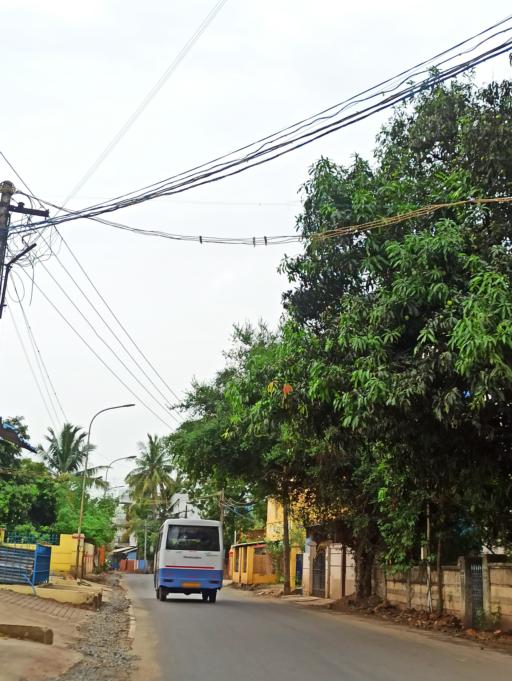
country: IN
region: Tamil Nadu
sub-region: Thiruvallur
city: Chinnasekkadu
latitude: 13.1672
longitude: 80.2396
